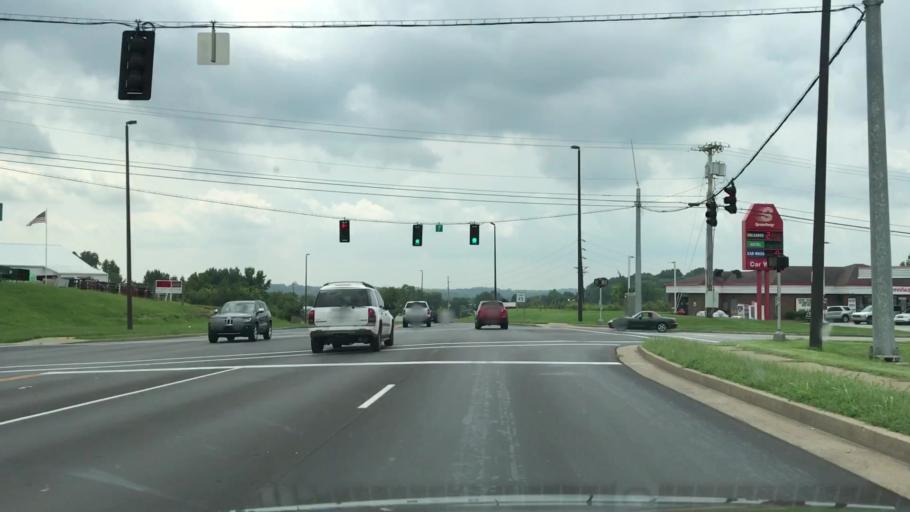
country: US
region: Kentucky
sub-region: Barren County
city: Glasgow
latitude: 36.9961
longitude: -85.9306
